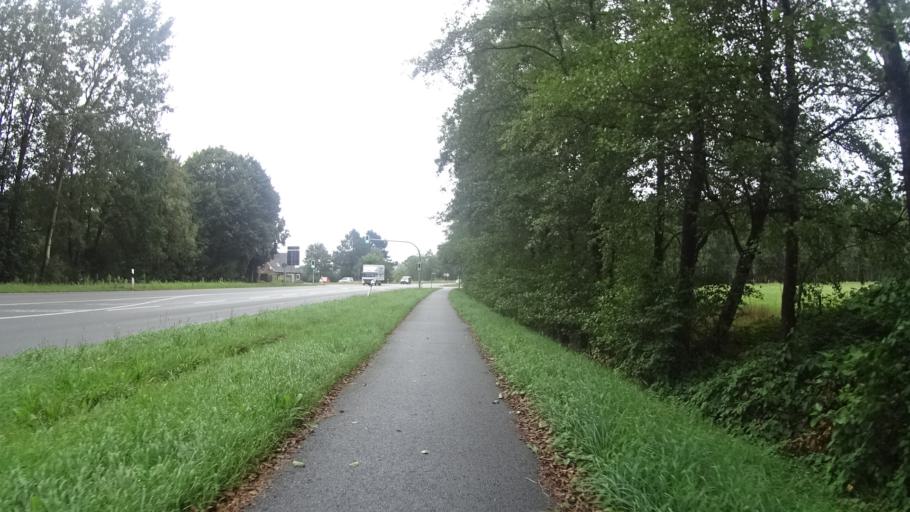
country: DE
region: Lower Saxony
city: Brinkum
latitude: 53.2663
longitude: 7.5473
